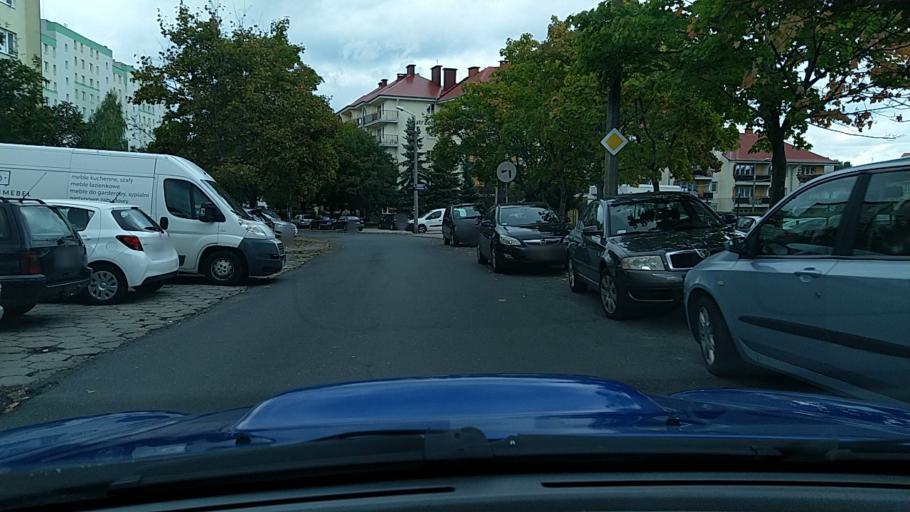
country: PL
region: Warmian-Masurian Voivodeship
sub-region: Olsztyn
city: Kortowo
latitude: 53.7409
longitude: 20.4820
